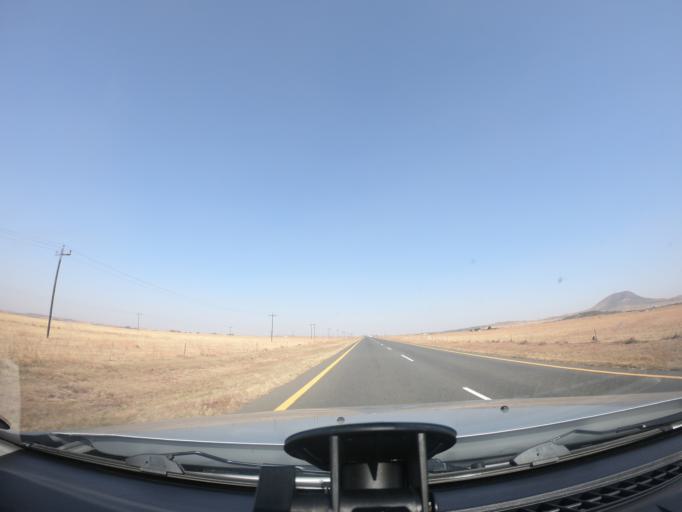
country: ZA
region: KwaZulu-Natal
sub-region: uThukela District Municipality
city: Ekuvukeni
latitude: -28.3728
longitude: 29.9490
